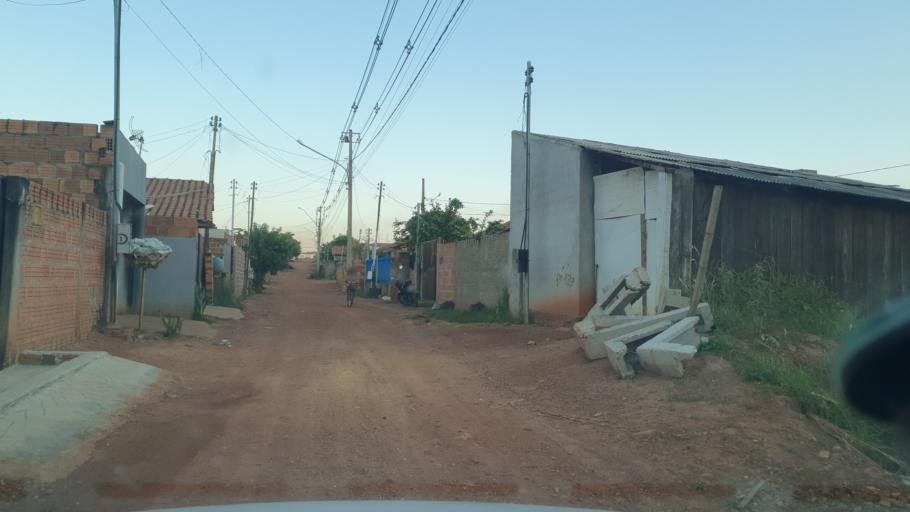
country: BR
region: Mato Grosso
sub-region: Pontes E Lacerda
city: Pontes e Lacerda
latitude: -15.2215
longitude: -59.3199
